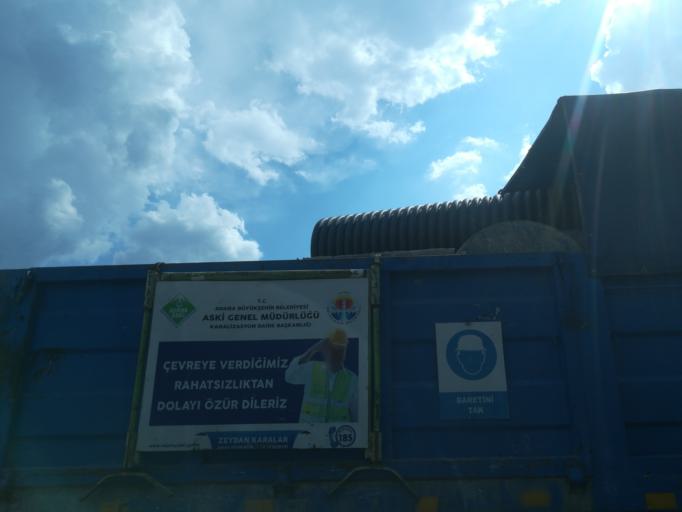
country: TR
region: Adana
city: Adana
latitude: 36.9899
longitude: 35.3313
